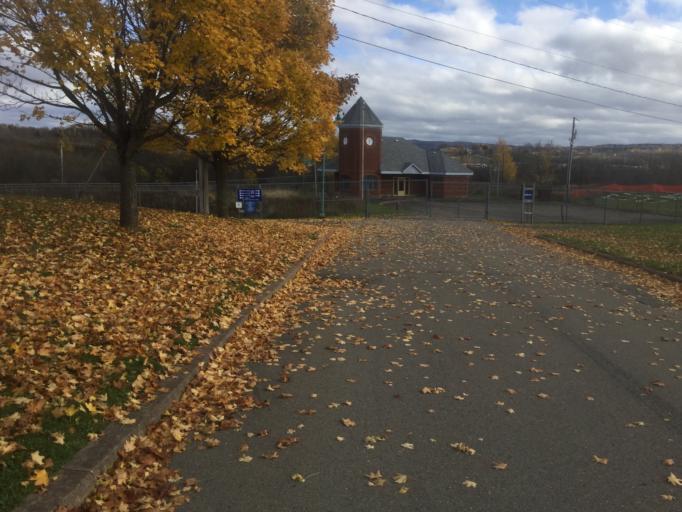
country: CA
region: Nova Scotia
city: New Glasgow
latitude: 45.5683
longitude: -62.6564
